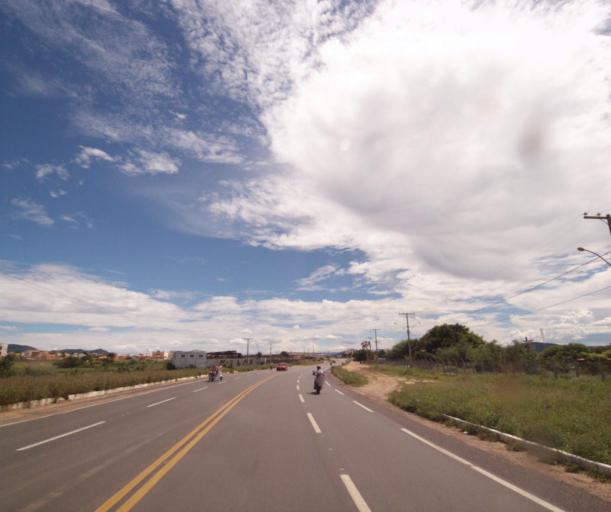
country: BR
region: Bahia
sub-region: Guanambi
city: Guanambi
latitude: -14.2245
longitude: -42.7629
